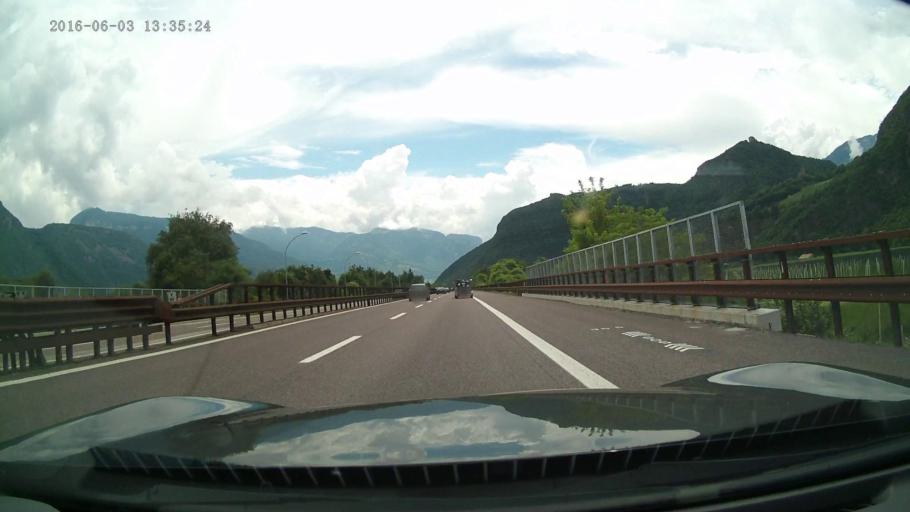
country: IT
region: Trentino-Alto Adige
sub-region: Bolzano
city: Vadena
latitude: 46.3891
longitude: 11.2940
